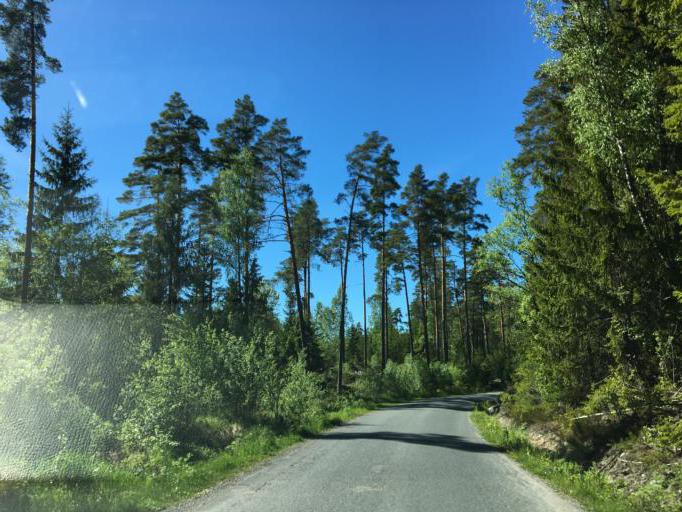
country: SE
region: Soedermanland
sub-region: Eskilstuna Kommun
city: Hallbybrunn
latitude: 59.3513
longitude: 16.3926
